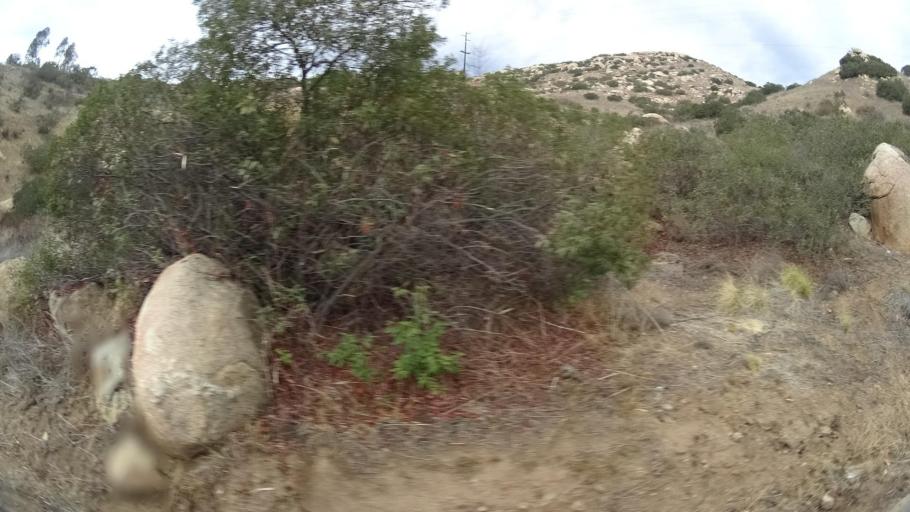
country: US
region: California
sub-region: San Diego County
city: San Pasqual
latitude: 33.0640
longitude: -117.0280
